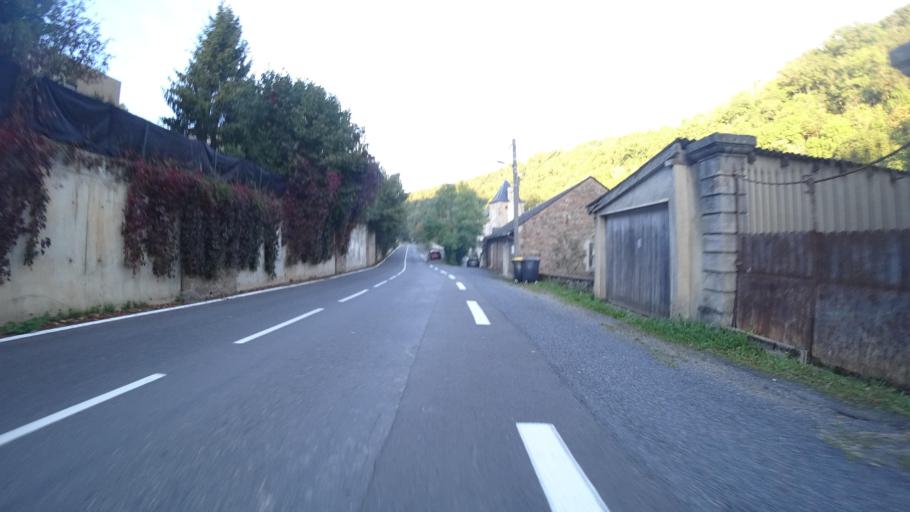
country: FR
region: Midi-Pyrenees
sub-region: Departement de l'Aveyron
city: Le Monastere
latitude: 44.3466
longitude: 2.5820
